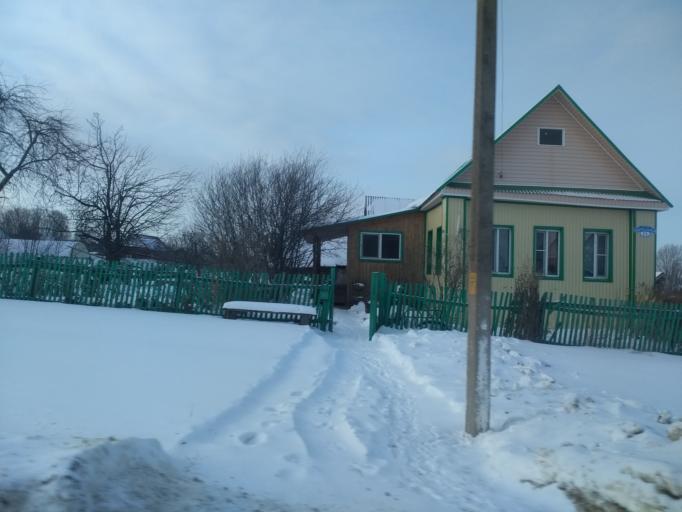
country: RU
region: Bashkortostan
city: Iglino
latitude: 54.7743
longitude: 56.5366
